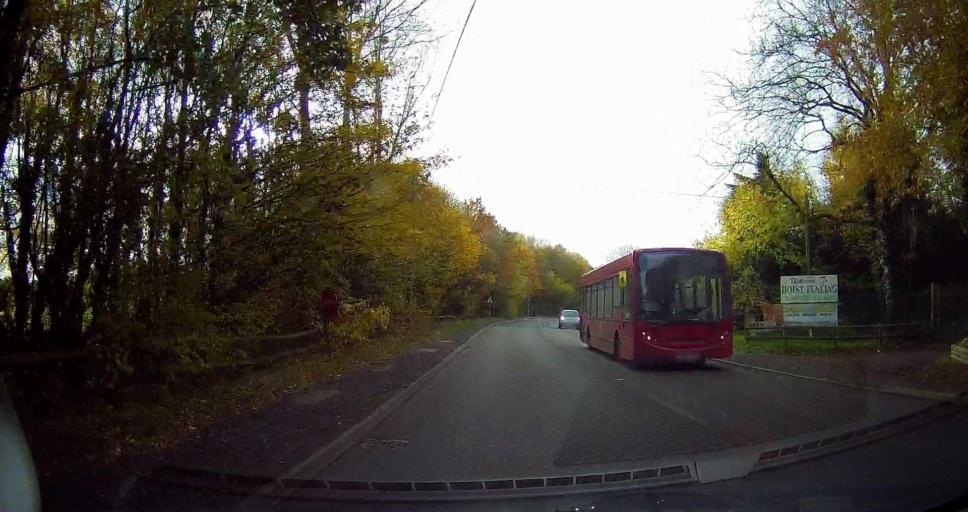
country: GB
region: England
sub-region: Kent
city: Meopham
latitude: 51.3385
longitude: 0.3446
